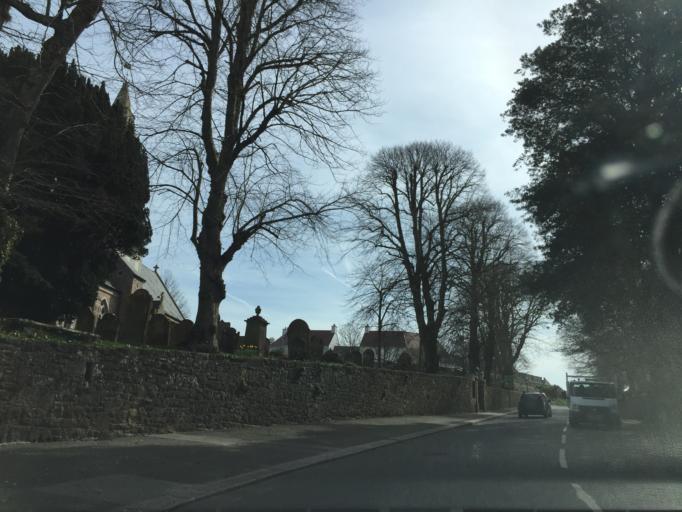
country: JE
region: St Helier
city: Saint Helier
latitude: 49.2335
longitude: -2.0924
